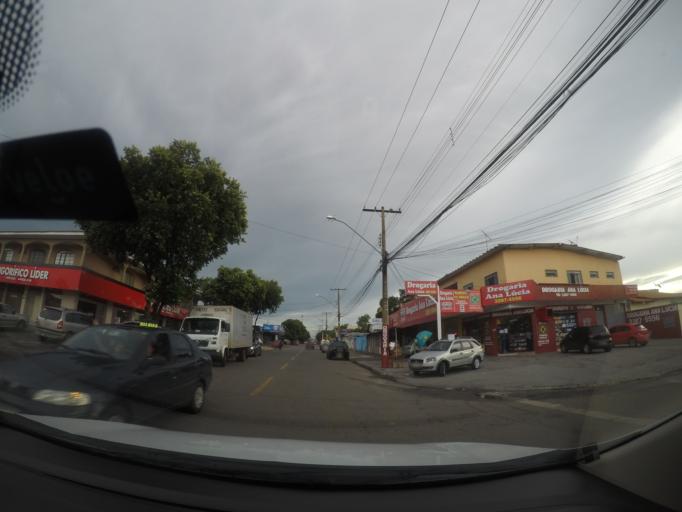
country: BR
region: Goias
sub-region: Goiania
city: Goiania
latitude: -16.7014
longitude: -49.3076
